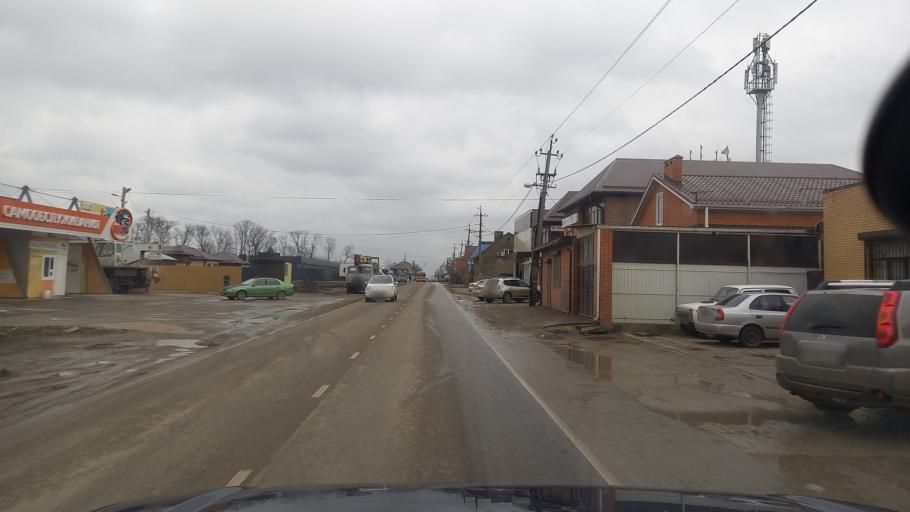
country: RU
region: Krasnodarskiy
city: Pashkovskiy
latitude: 45.0593
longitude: 39.1713
